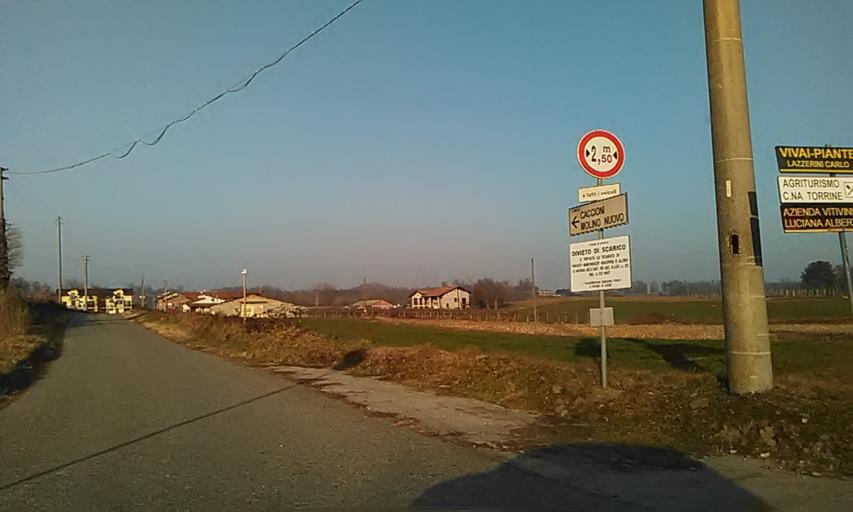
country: IT
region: Piedmont
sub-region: Provincia di Biella
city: Cavaglia
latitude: 45.4086
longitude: 8.1000
